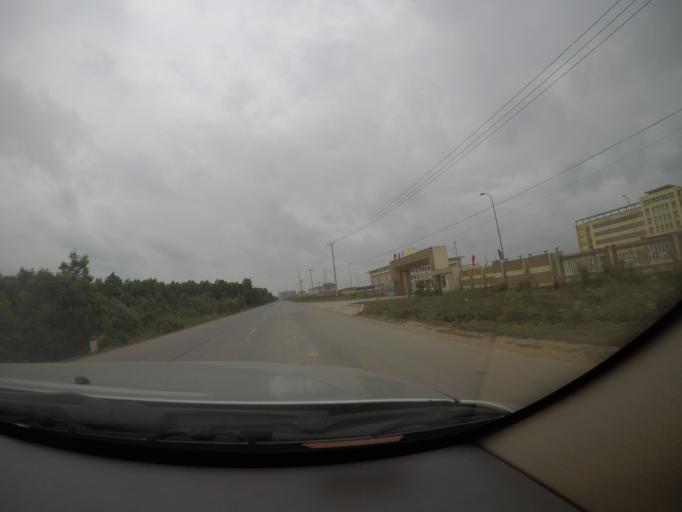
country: VN
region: Quang Tri
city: Dong Ha
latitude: 16.7906
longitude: 107.0968
